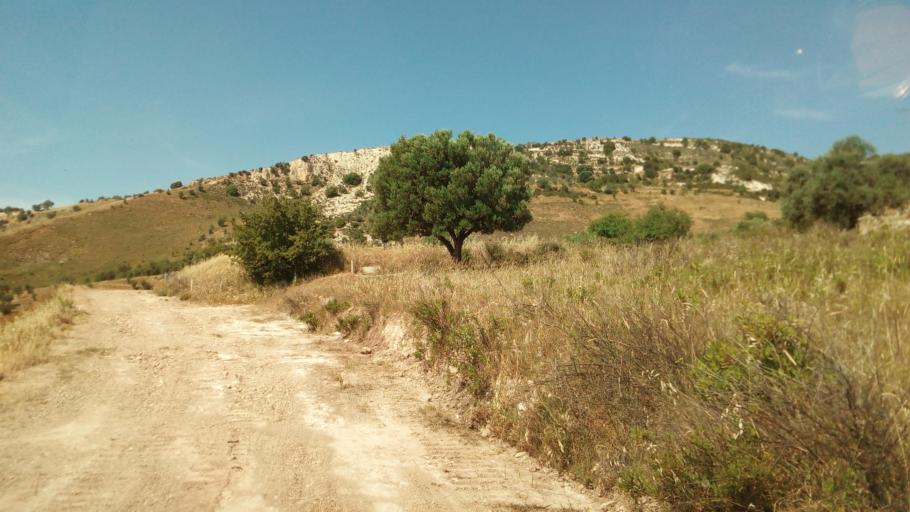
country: CY
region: Limassol
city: Pachna
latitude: 34.8215
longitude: 32.6993
